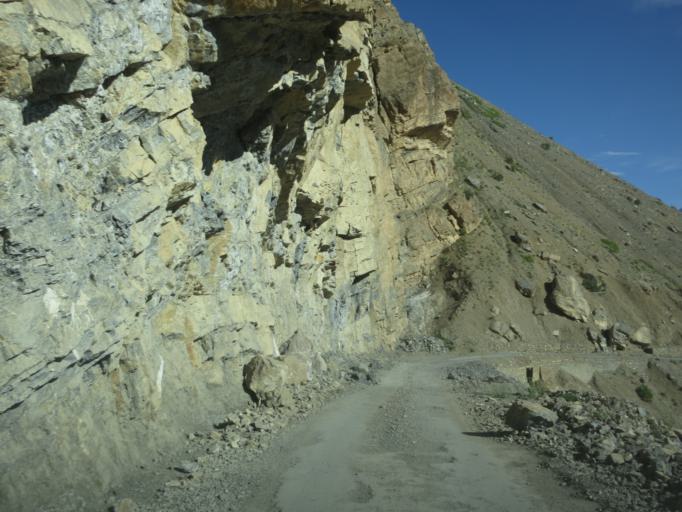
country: IN
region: Himachal Pradesh
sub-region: Shimla
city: Sarahan
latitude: 32.3124
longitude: 78.0036
